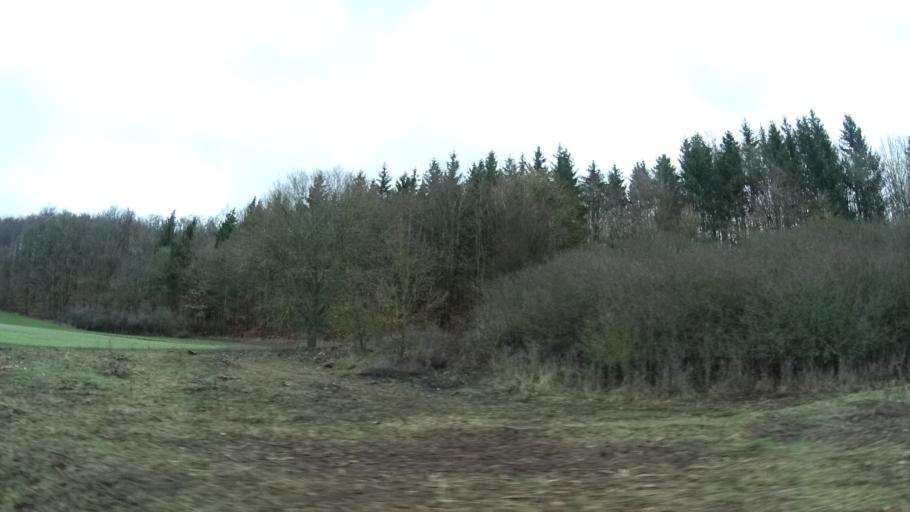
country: DE
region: Bavaria
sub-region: Regierungsbezirk Unterfranken
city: Willmars
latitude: 50.5478
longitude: 10.2333
